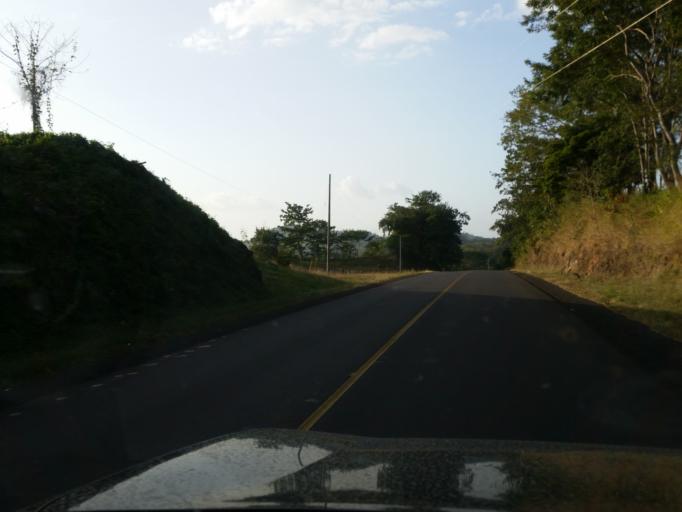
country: NI
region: Rio San Juan
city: San Miguelito
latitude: 11.3920
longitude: -84.8004
